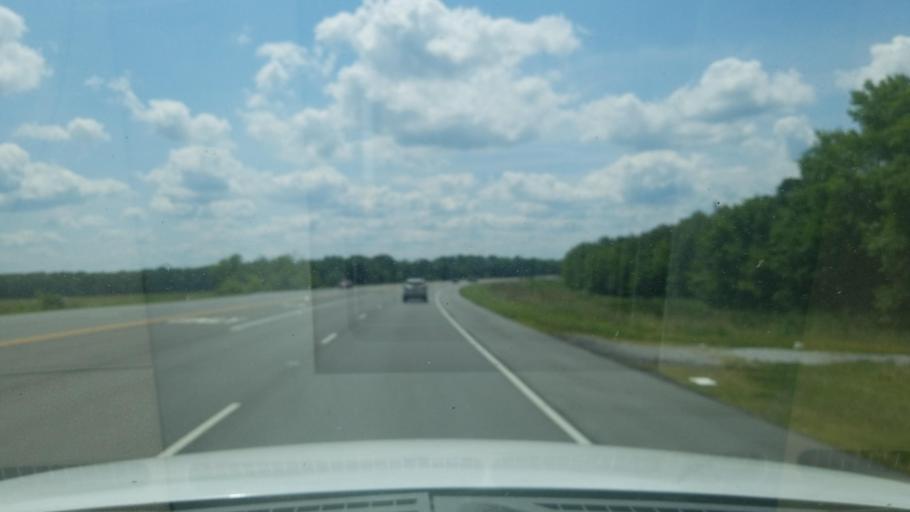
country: US
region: Illinois
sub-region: Saline County
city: Harrisburg
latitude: 37.7581
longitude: -88.5155
